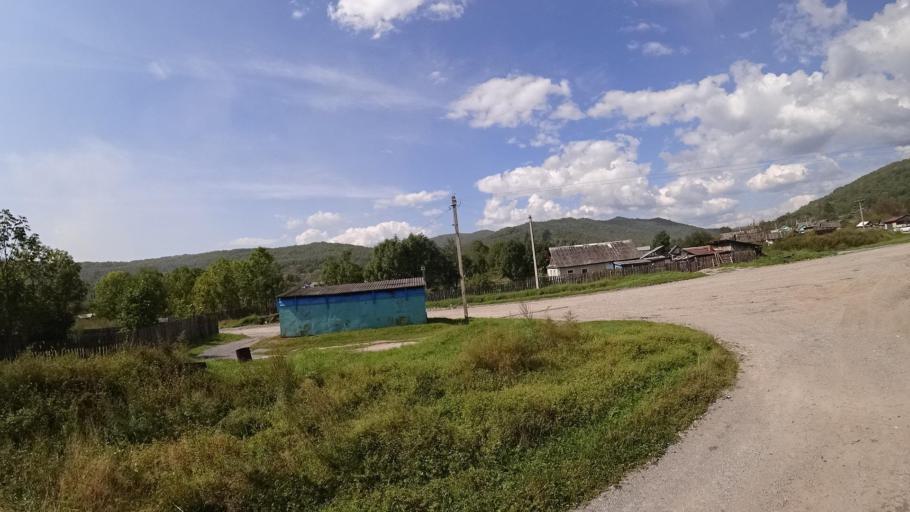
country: RU
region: Jewish Autonomous Oblast
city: Londoko
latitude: 49.0257
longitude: 131.9323
